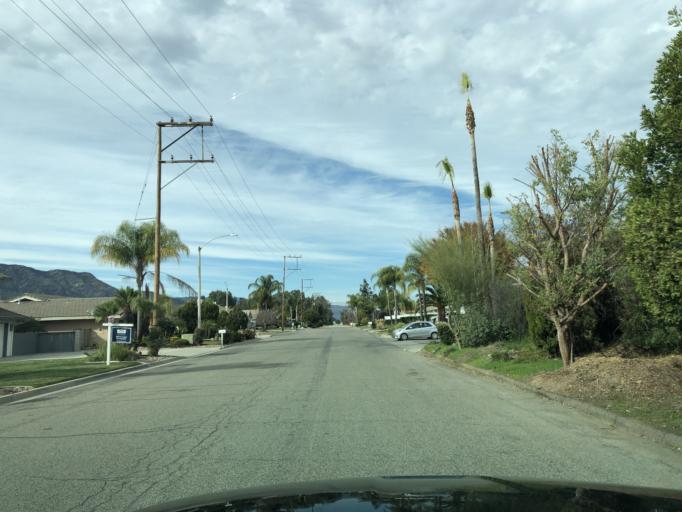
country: US
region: California
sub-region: Riverside County
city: Wildomar
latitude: 33.6108
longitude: -117.2918
